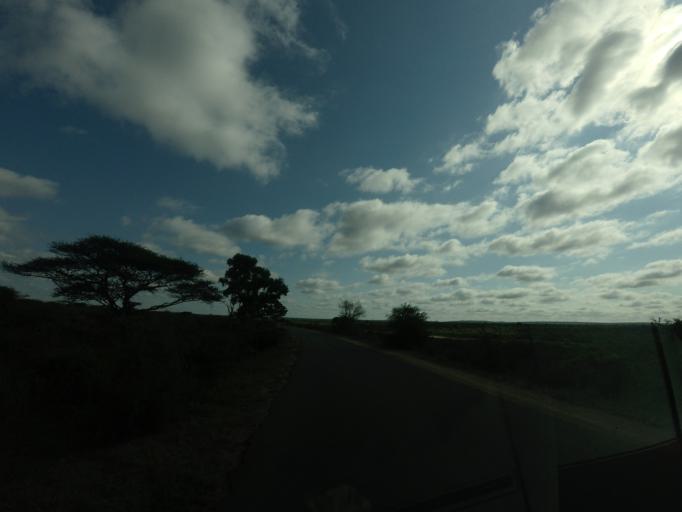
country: ZA
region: Mpumalanga
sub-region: Ehlanzeni District
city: Komatipoort
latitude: -25.1523
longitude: 31.9392
